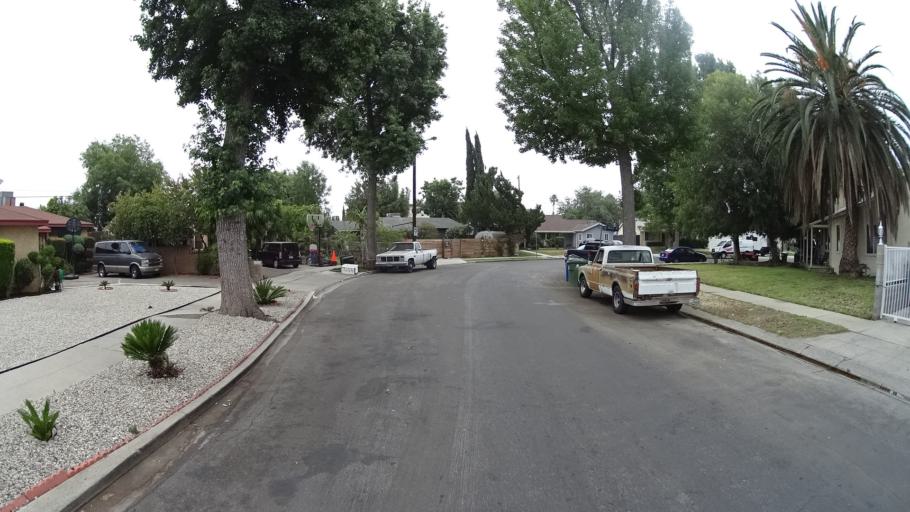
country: US
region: California
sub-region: Los Angeles County
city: Van Nuys
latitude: 34.1931
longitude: -118.4152
